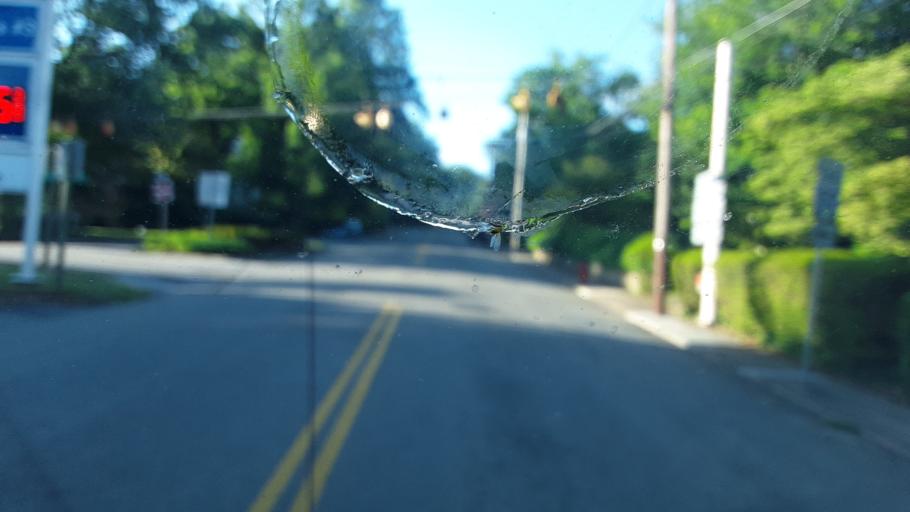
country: US
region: Virginia
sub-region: Pittsylvania County
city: Chatham
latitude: 36.8228
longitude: -79.3971
